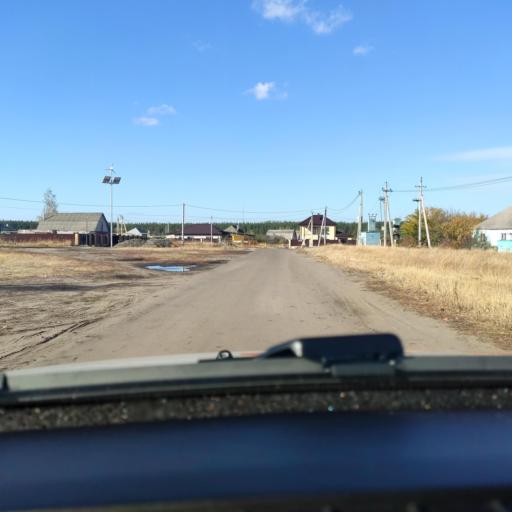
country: RU
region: Voronezj
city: Shilovo
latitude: 51.5201
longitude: 39.1471
